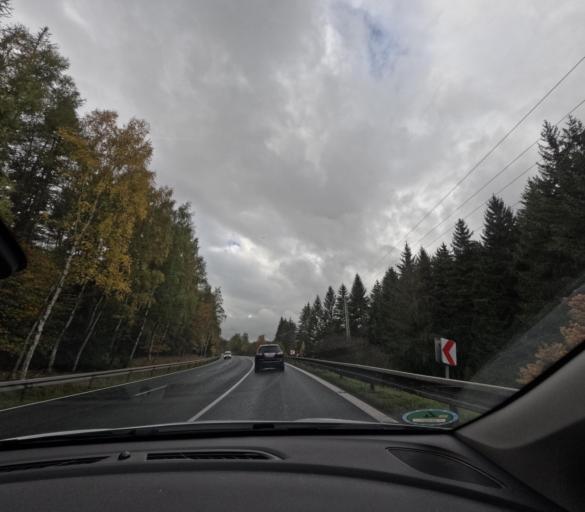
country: CZ
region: Karlovarsky
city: Dalovice
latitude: 50.2345
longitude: 12.9164
